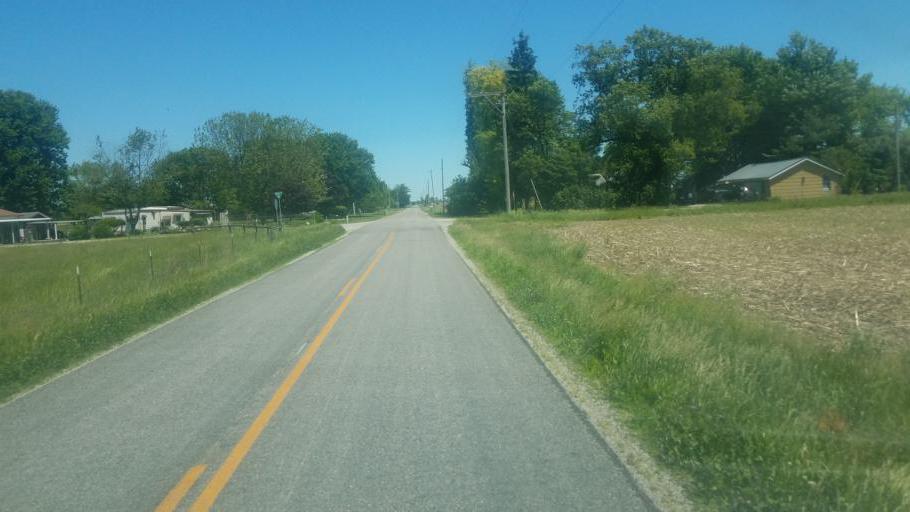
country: US
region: Ohio
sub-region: Shelby County
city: Sidney
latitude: 40.2124
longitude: -84.1349
